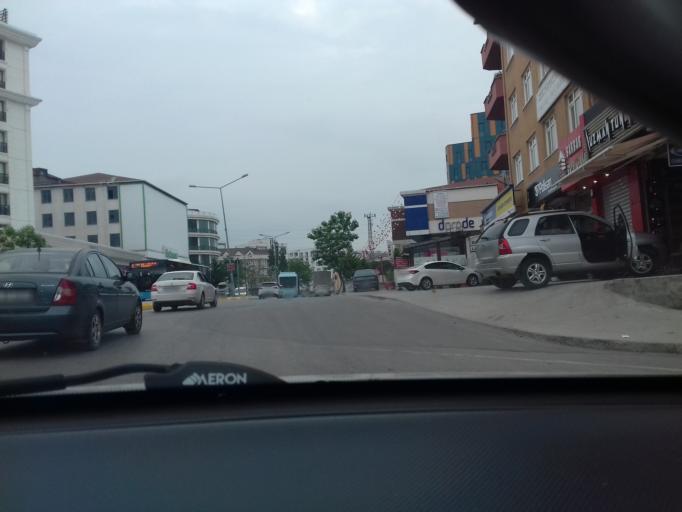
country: TR
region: Istanbul
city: Pendik
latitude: 40.9119
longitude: 29.2988
